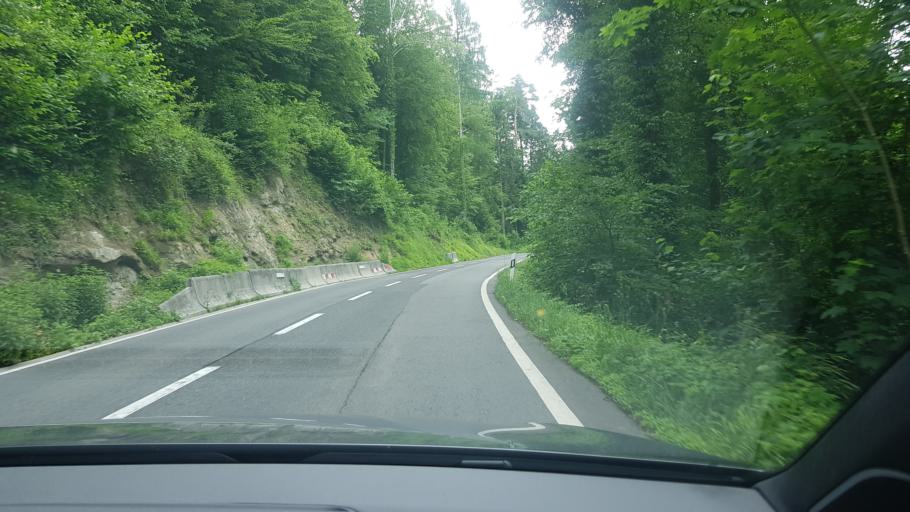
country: CH
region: Zug
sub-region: Zug
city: Baar
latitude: 47.1952
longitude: 8.5427
